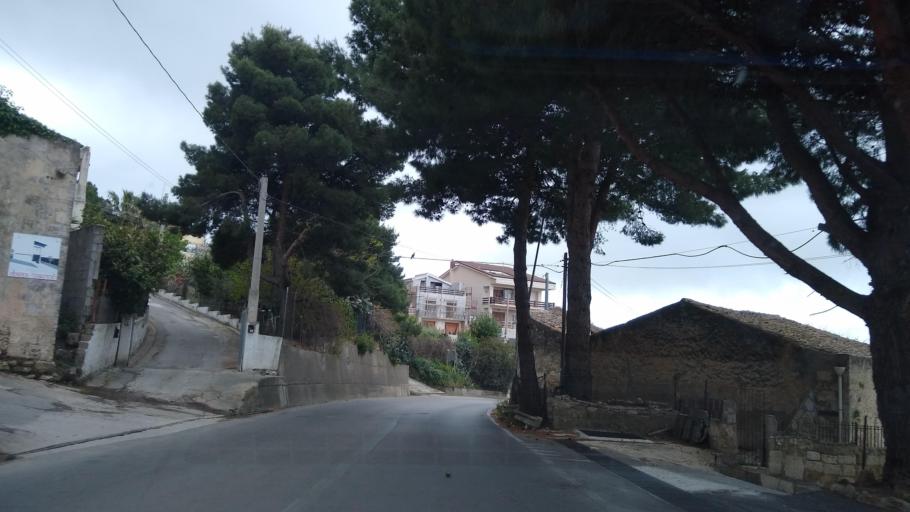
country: IT
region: Sicily
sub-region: Trapani
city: Alcamo
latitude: 37.9784
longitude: 12.9466
